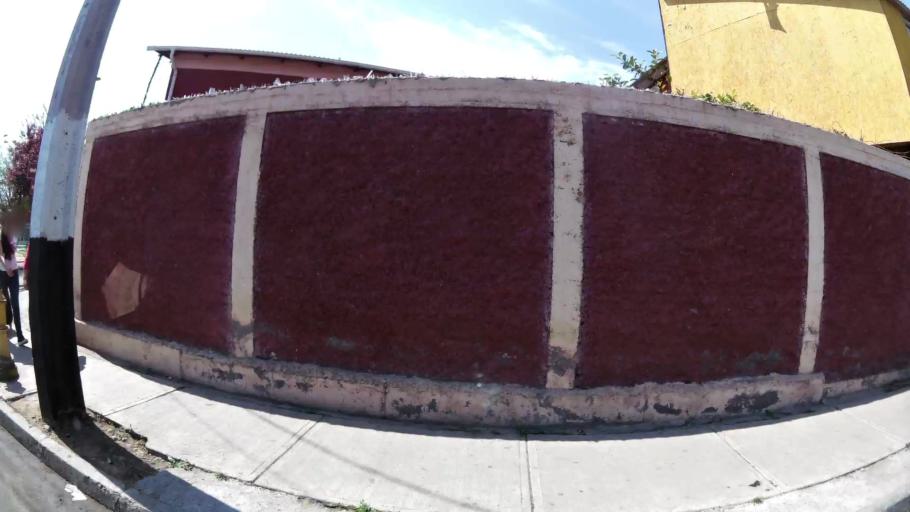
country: CL
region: Santiago Metropolitan
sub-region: Provincia de Santiago
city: La Pintana
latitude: -33.5894
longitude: -70.6099
